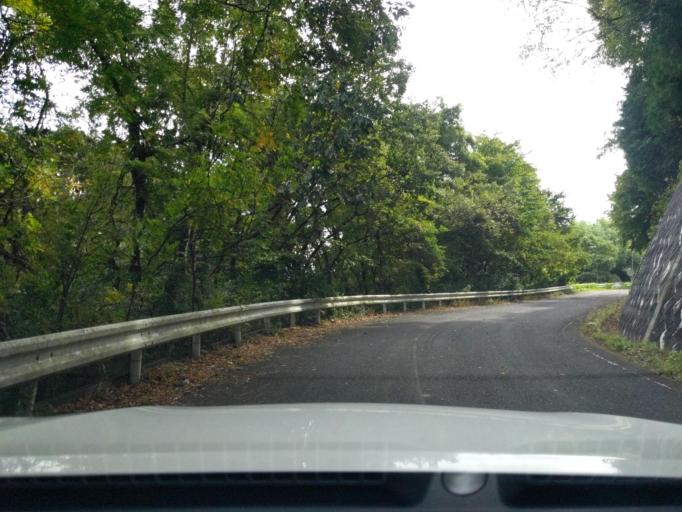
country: JP
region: Fukushima
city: Koriyama
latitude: 37.4095
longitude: 140.2771
